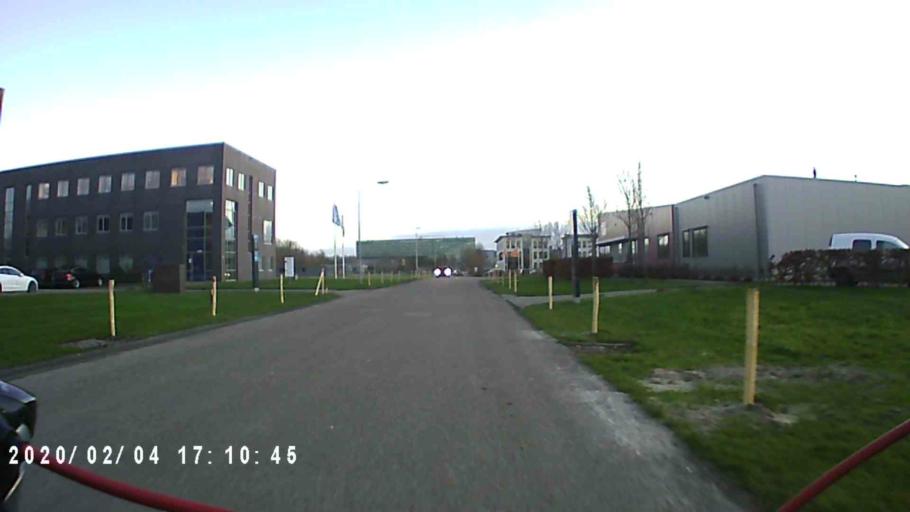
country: NL
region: Groningen
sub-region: Gemeente Groningen
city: Korrewegwijk
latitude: 53.2463
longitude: 6.5337
